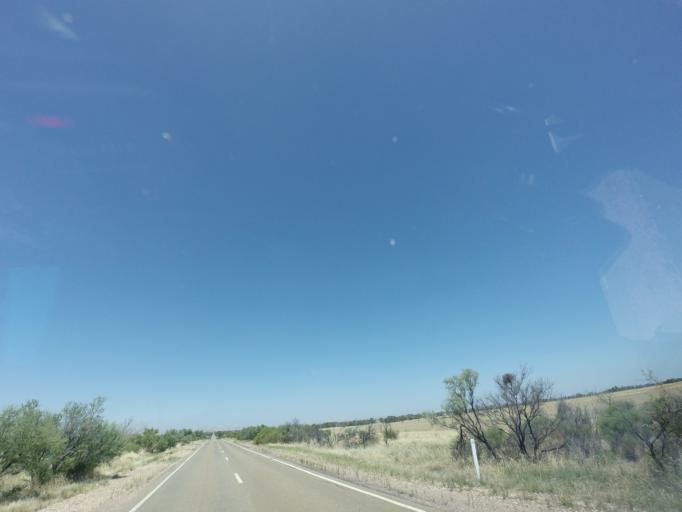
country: AU
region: South Australia
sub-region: Flinders Ranges
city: Quorn
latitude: -32.6662
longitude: 138.1333
